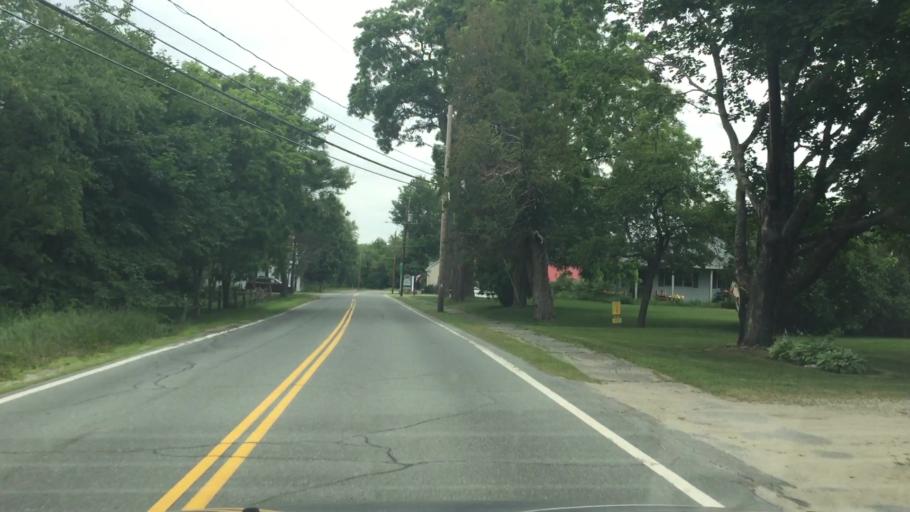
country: US
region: New Hampshire
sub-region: Grafton County
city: Littleton
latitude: 44.2332
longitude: -71.7565
